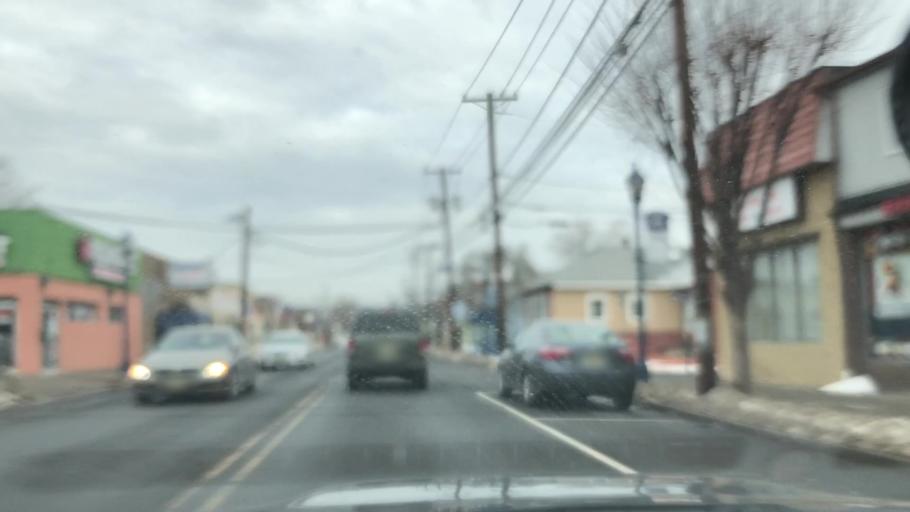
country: US
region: New Jersey
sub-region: Somerset County
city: South Bound Brook
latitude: 40.5538
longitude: -74.5249
